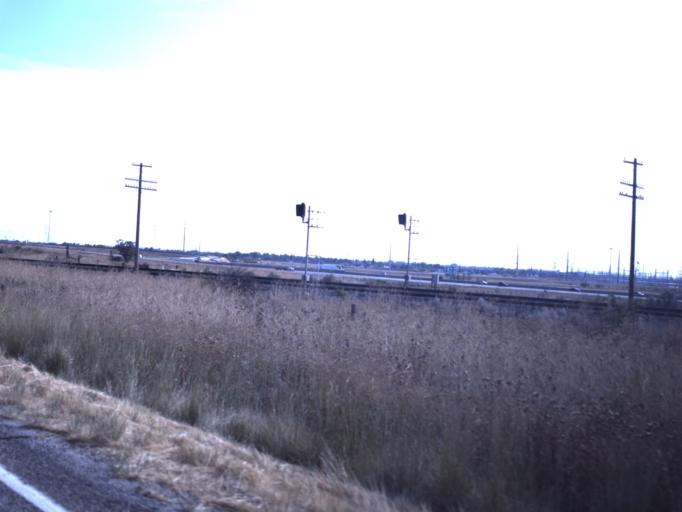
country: US
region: Utah
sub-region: Box Elder County
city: South Willard
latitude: 41.3479
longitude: -112.0364
